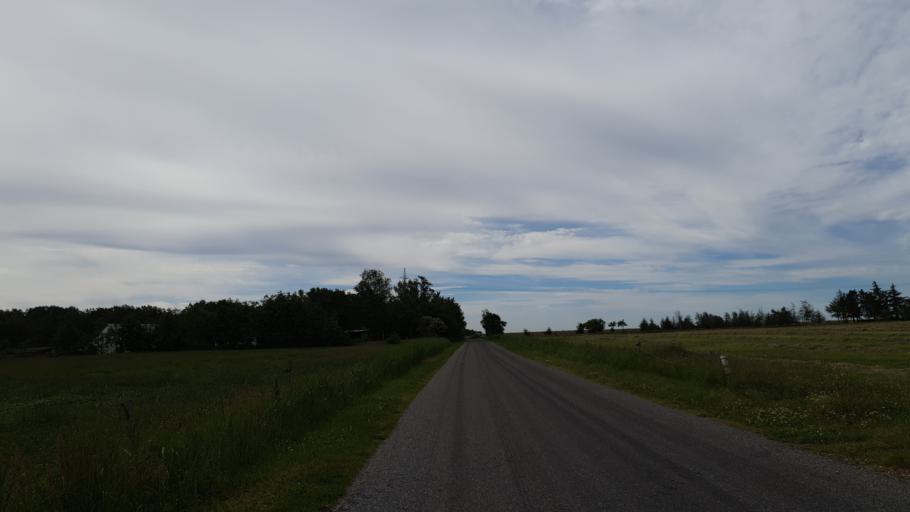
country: DK
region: North Denmark
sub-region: Laeso Kommune
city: Byrum
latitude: 57.2470
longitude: 10.9853
